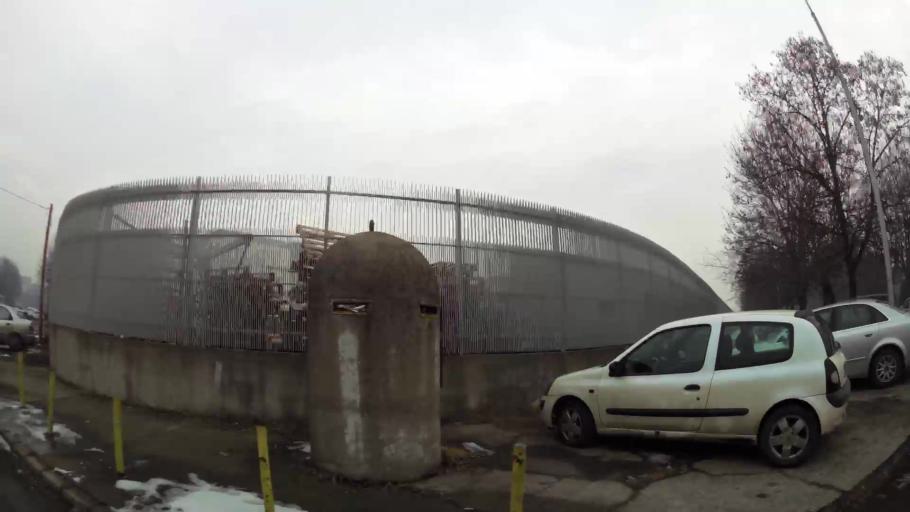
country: MK
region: Cair
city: Cair
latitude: 41.9994
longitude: 21.4655
